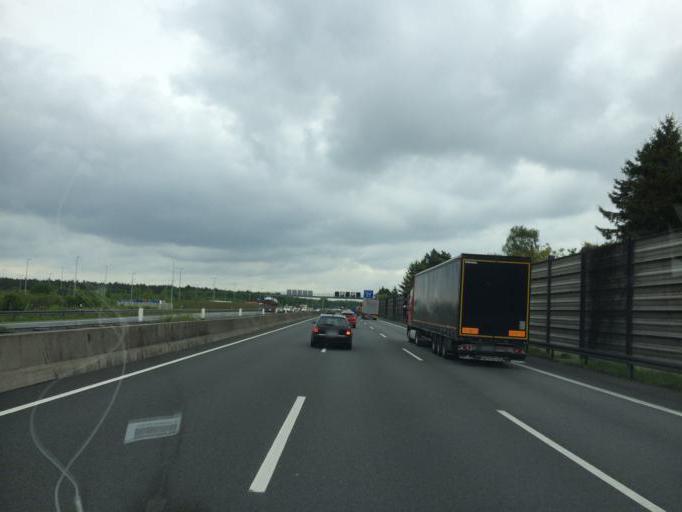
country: DE
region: Lower Saxony
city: Lehrte
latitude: 52.3890
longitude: 9.9847
